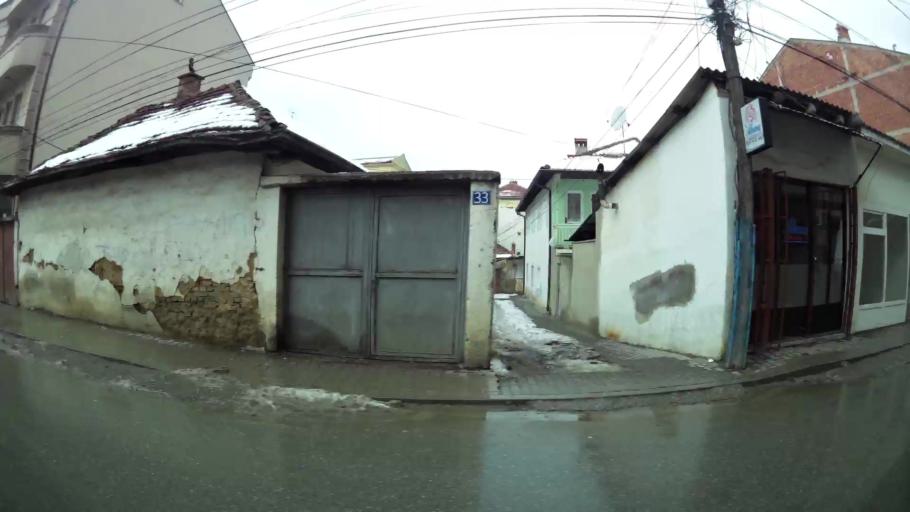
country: XK
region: Pristina
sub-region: Komuna e Prishtines
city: Pristina
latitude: 42.6686
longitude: 21.1696
